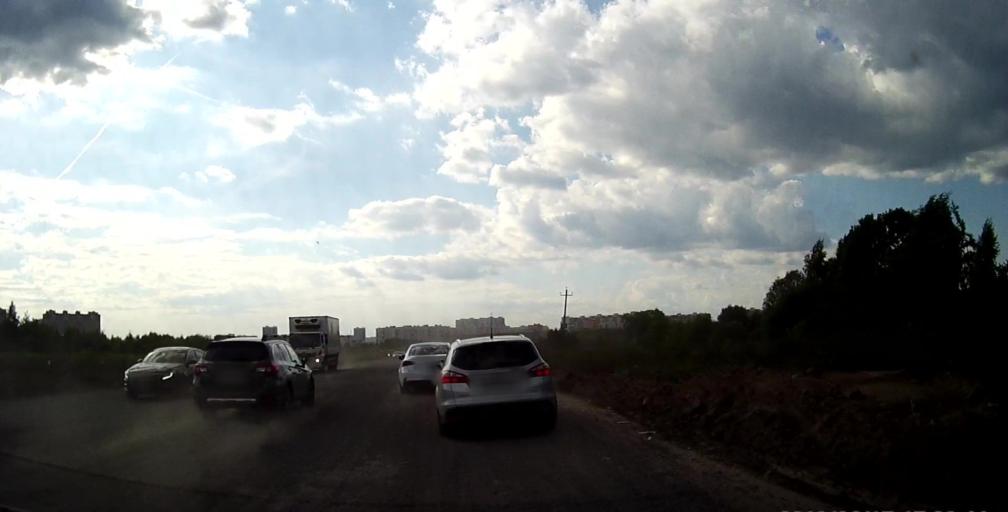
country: RU
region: Moskovskaya
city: Shcherbinka
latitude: 55.5238
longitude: 37.5308
